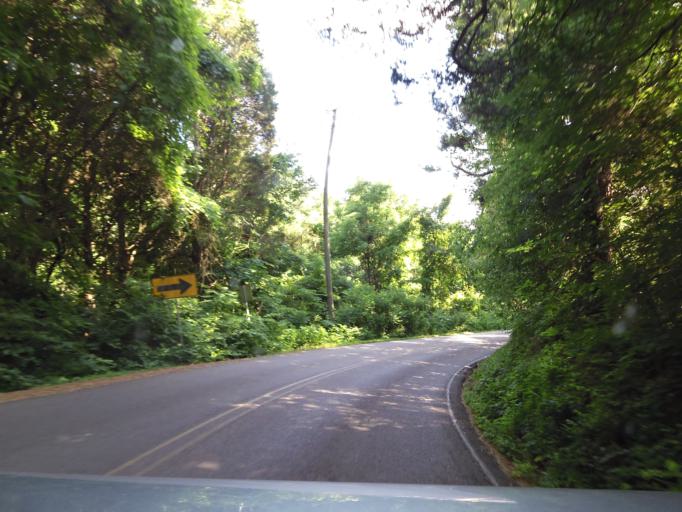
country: US
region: Tennessee
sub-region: Knox County
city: Knoxville
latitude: 36.0845
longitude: -83.8986
